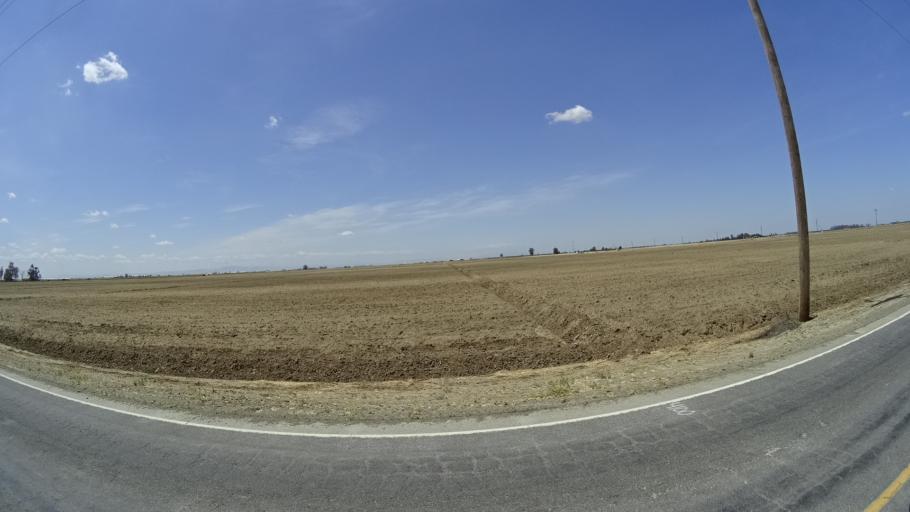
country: US
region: California
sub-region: Kings County
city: Home Garden
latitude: 36.2226
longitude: -119.6549
